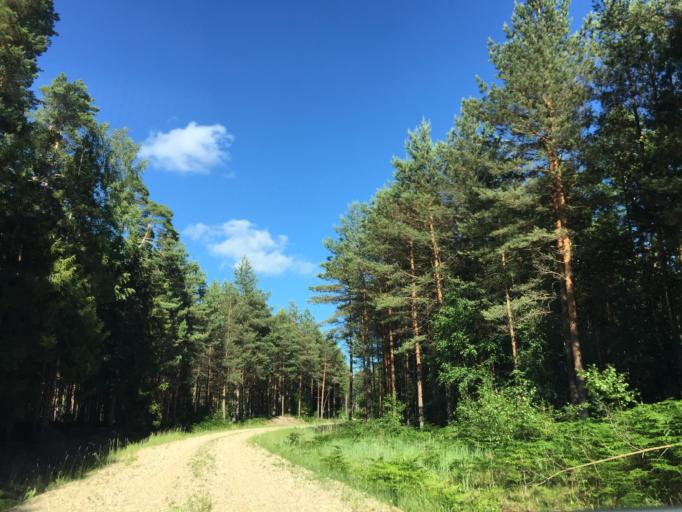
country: LV
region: Ventspils
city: Ventspils
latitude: 57.5397
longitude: 21.7429
